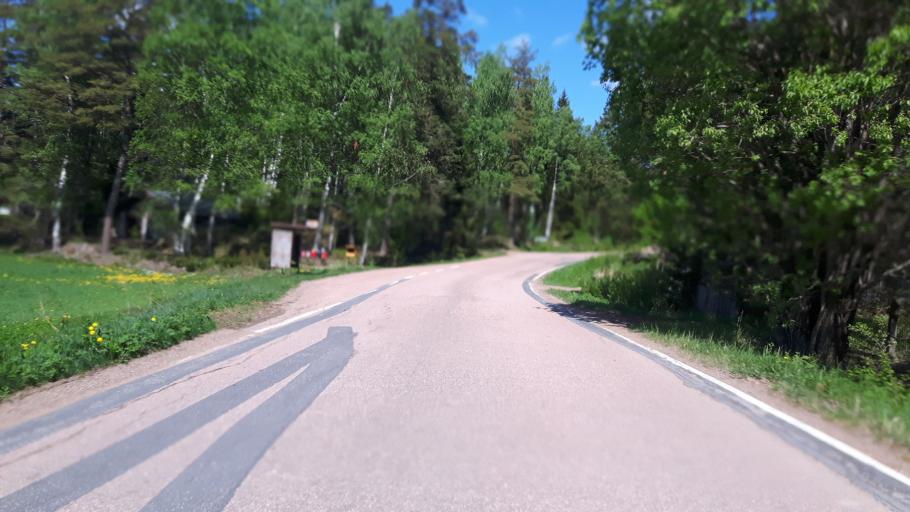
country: FI
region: Kymenlaakso
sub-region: Kotka-Hamina
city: Virolahti
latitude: 60.5353
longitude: 27.6162
